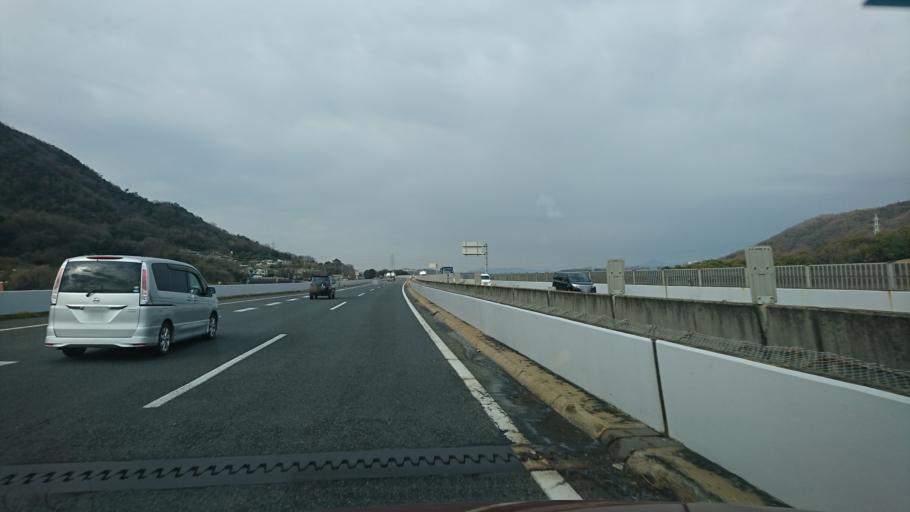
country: JP
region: Hiroshima
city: Fukuyama
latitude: 34.5144
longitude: 133.3926
